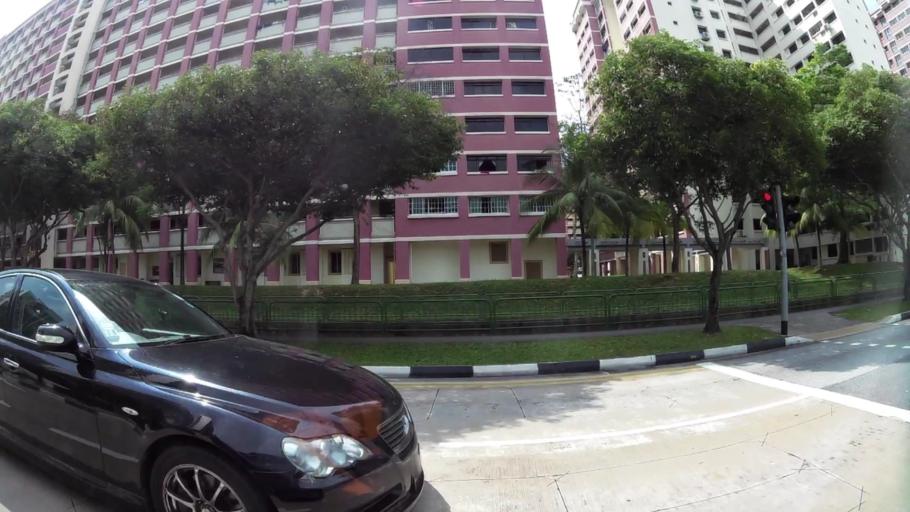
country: SG
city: Singapore
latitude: 1.3573
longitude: 103.9381
